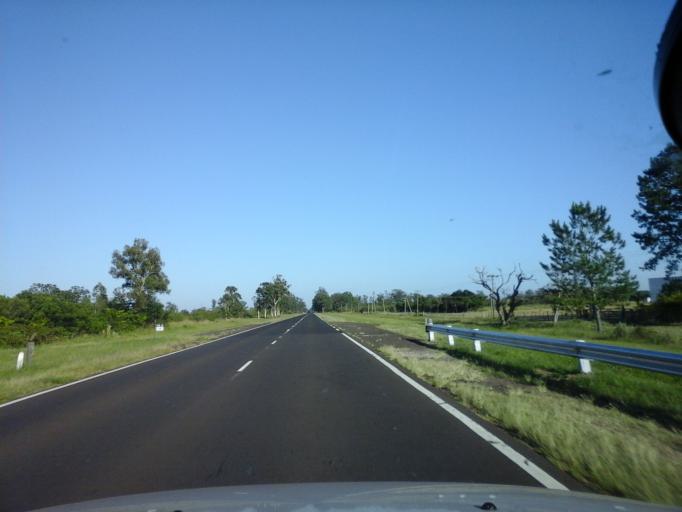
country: AR
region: Corrientes
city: Ita Ibate
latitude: -27.4610
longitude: -57.3157
